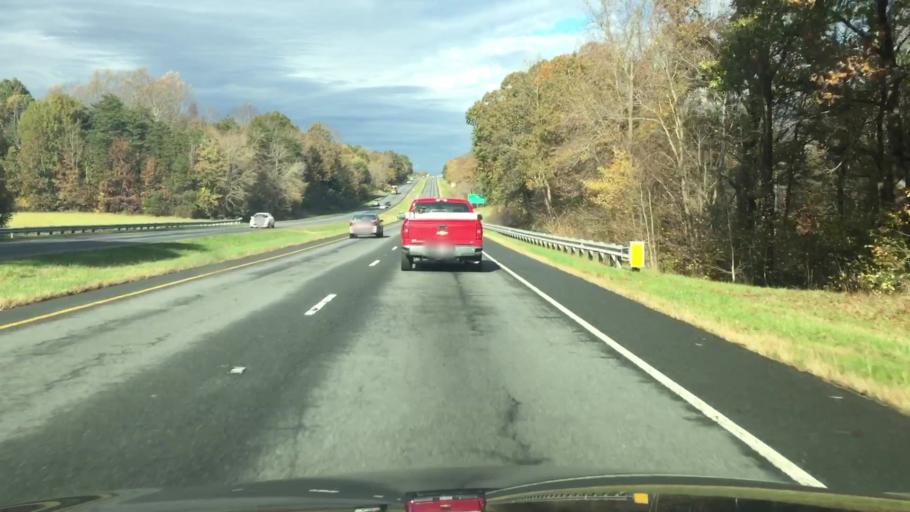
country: US
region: North Carolina
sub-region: Guilford County
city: McLeansville
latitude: 36.2021
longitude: -79.6955
